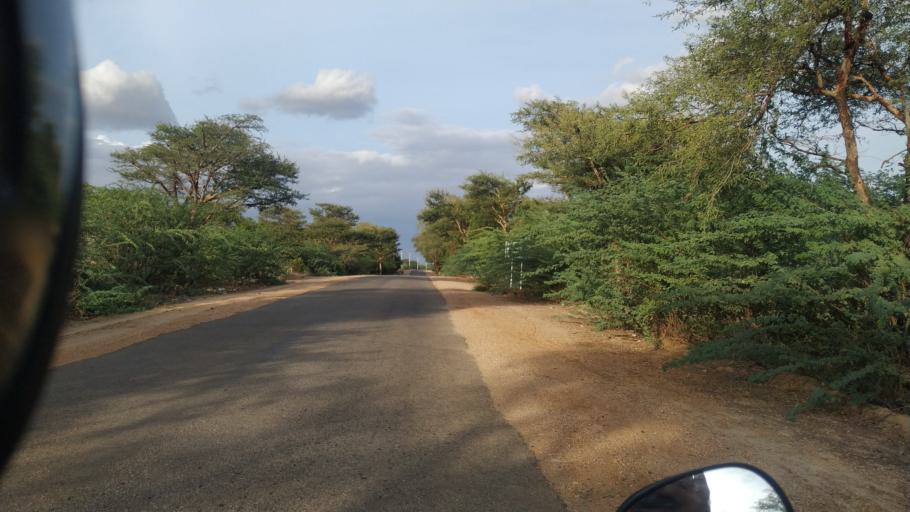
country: MM
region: Magway
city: Pakokku
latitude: 21.3560
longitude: 94.9065
